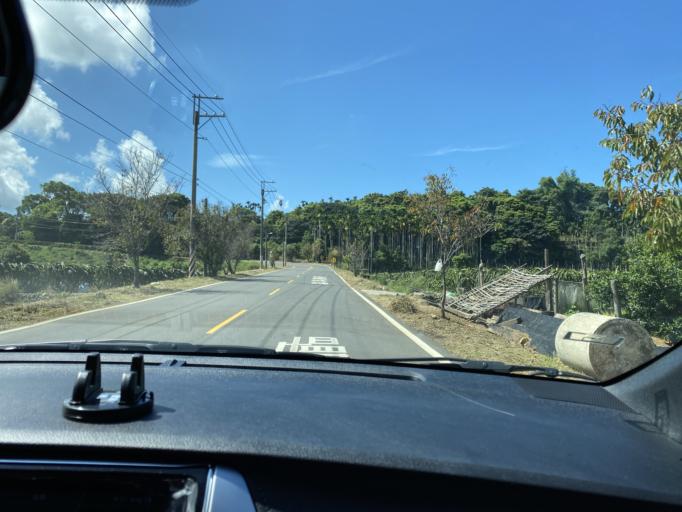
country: TW
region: Taiwan
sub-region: Nantou
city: Nantou
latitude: 23.8668
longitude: 120.6323
